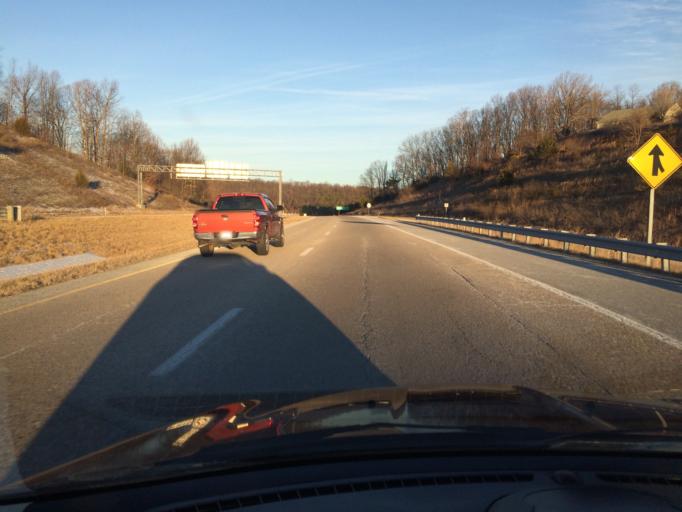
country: US
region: Virginia
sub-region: Augusta County
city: Jolivue
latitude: 38.1229
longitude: -79.0683
